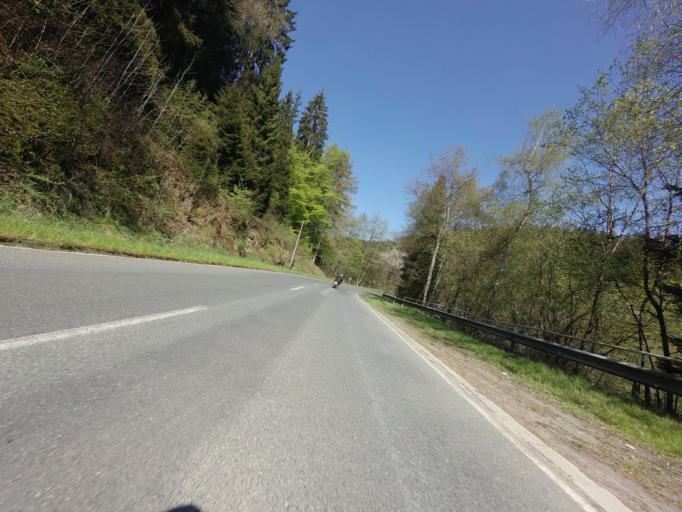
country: DE
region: North Rhine-Westphalia
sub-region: Regierungsbezirk Arnsberg
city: Olpe
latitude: 51.0862
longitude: 7.8219
